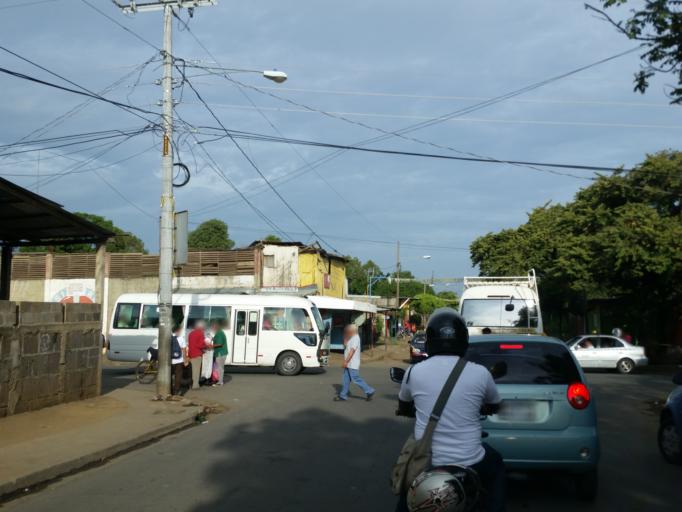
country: NI
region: Managua
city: Managua
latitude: 12.1052
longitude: -86.2234
